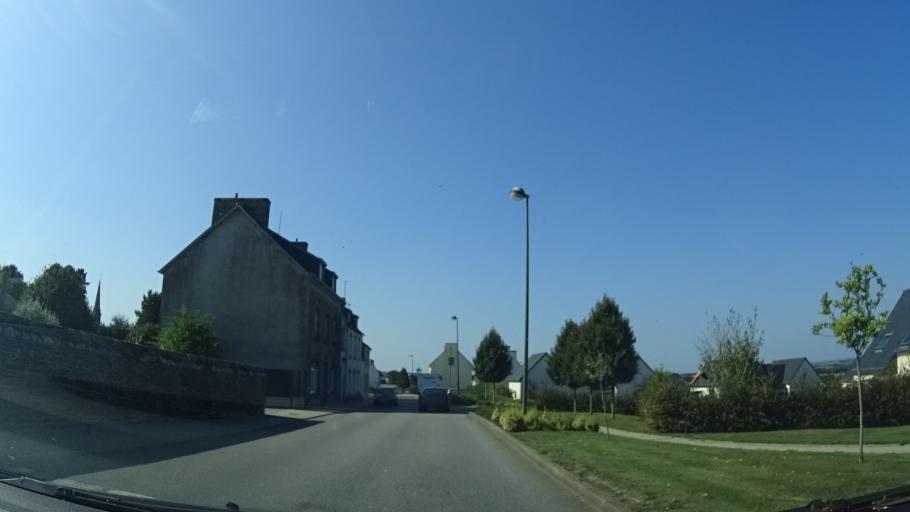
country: FR
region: Brittany
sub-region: Departement du Finistere
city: Cast
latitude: 48.1597
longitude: -4.1378
